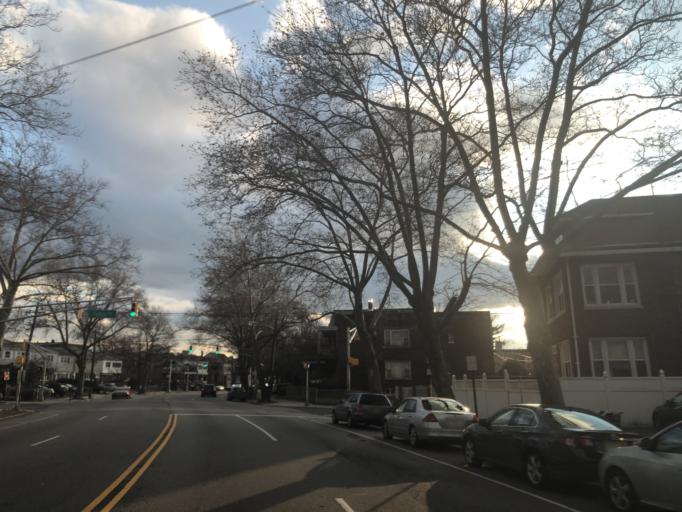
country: US
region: New Jersey
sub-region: Hudson County
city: Jersey City
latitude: 40.7066
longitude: -74.0890
